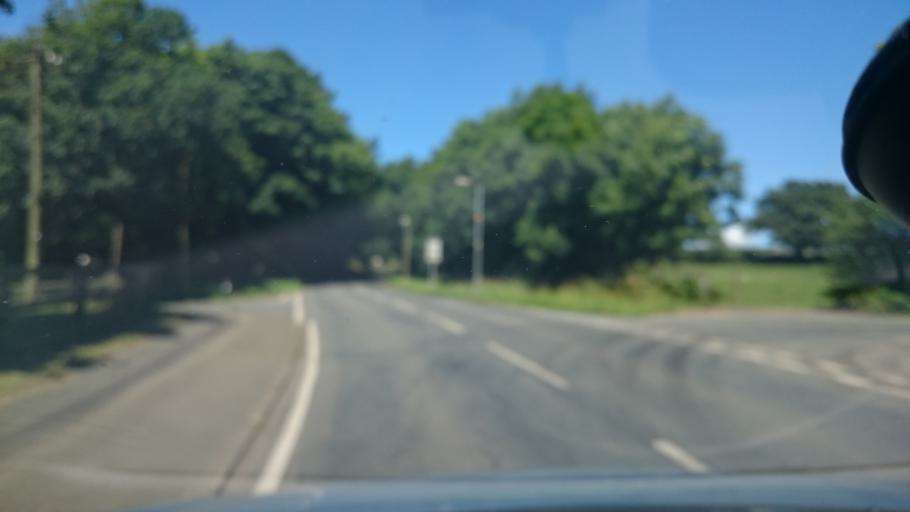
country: GB
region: Wales
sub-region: Pembrokeshire
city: Burton
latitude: 51.7279
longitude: -4.9209
